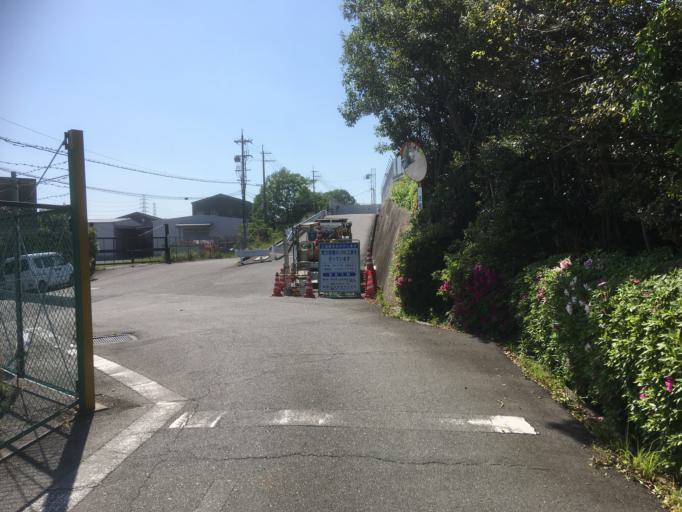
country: JP
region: Nara
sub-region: Ikoma-shi
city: Ikoma
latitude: 34.7330
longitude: 135.7145
